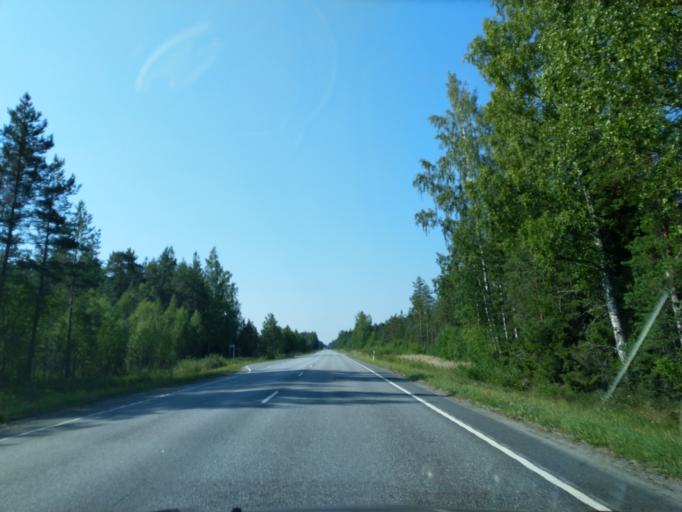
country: FI
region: Satakunta
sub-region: Pori
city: Pomarkku
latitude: 61.6806
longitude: 21.9883
